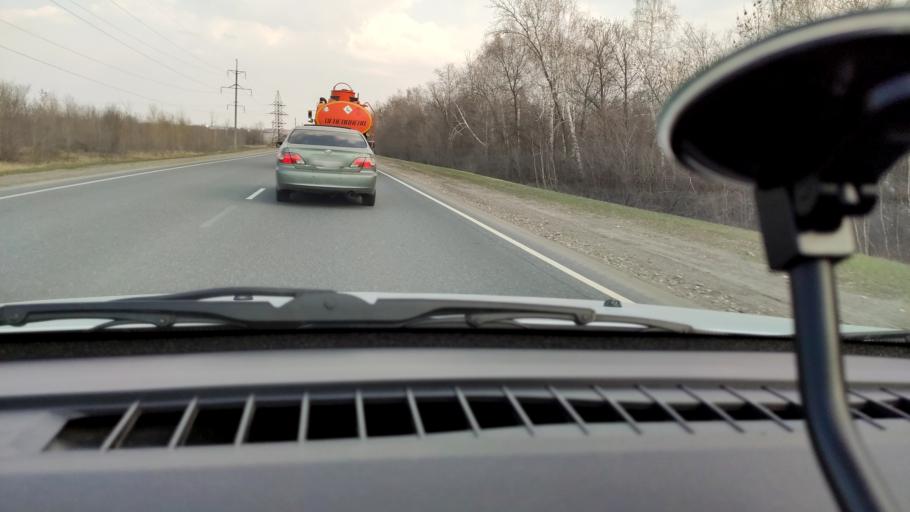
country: RU
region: Samara
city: Dubovyy Umet
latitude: 53.0905
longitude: 50.2986
